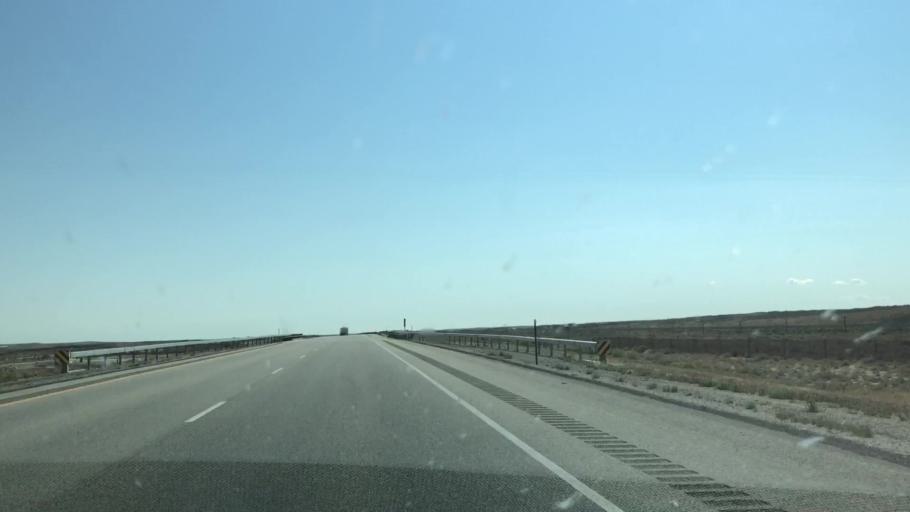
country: US
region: Wyoming
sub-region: Carbon County
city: Rawlins
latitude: 41.7032
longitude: -107.8509
